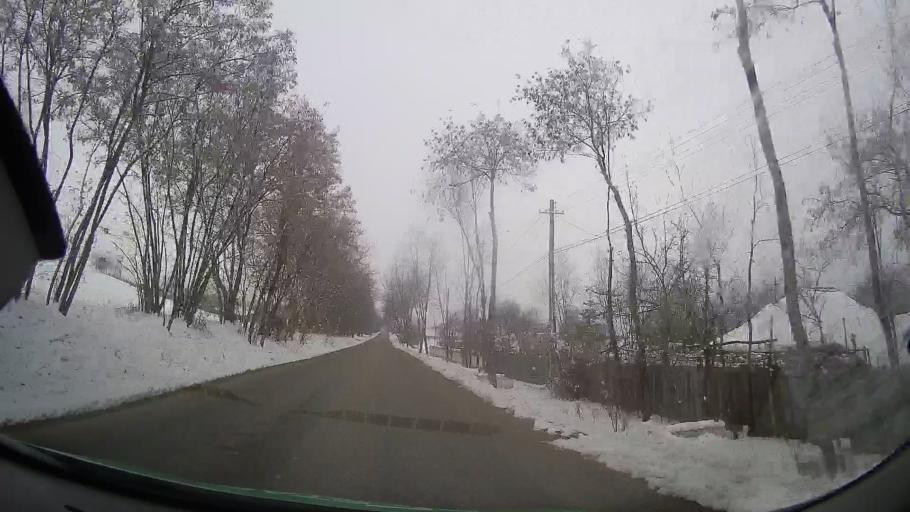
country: RO
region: Bacau
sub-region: Comuna Oncesti
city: Oncesti
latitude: 46.4393
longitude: 27.2673
